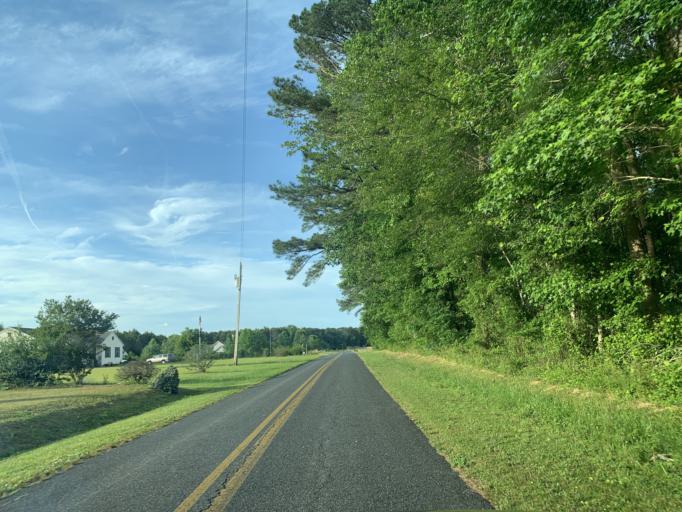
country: US
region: Maryland
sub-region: Worcester County
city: Pocomoke City
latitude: 38.0871
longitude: -75.4660
